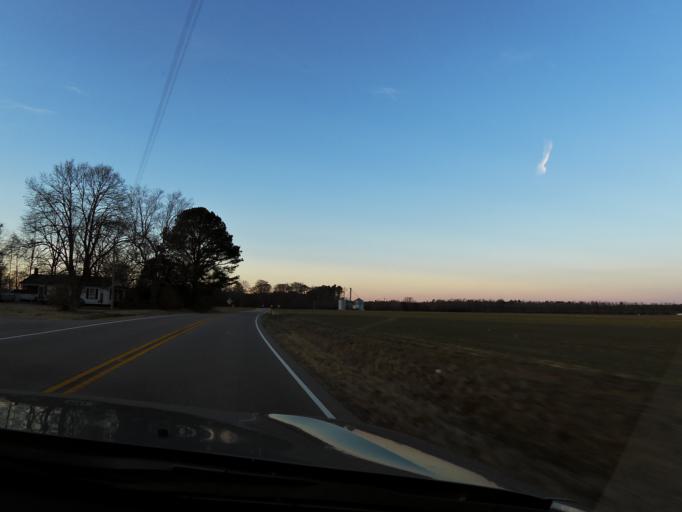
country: US
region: Virginia
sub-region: Southampton County
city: Courtland
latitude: 36.7289
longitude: -77.0727
